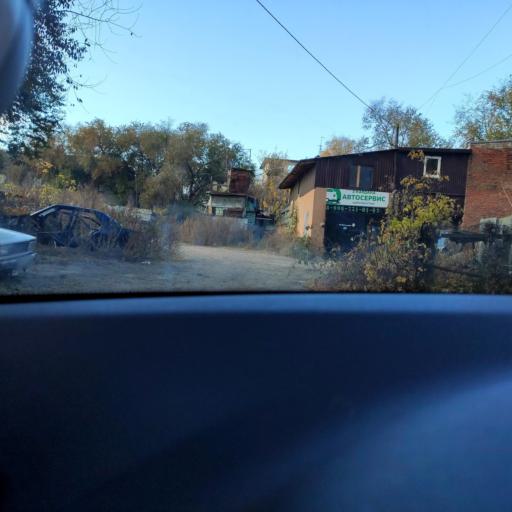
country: RU
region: Samara
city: Samara
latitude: 53.2176
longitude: 50.2323
